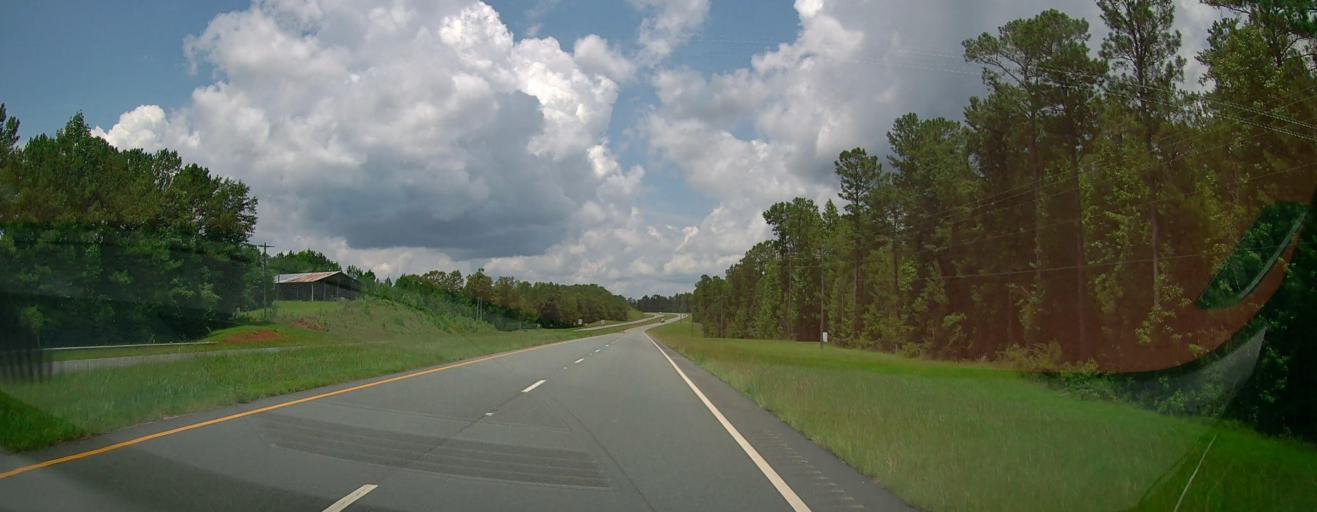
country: US
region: Georgia
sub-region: Upson County
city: Thomaston
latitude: 32.8098
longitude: -84.2840
